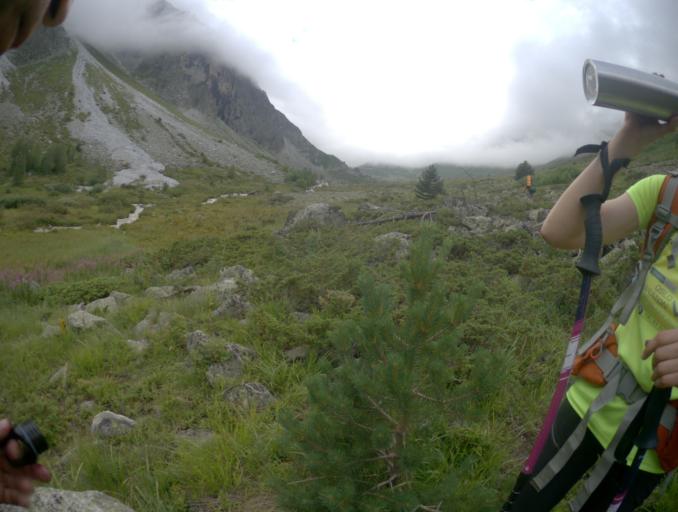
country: RU
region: Karachayevo-Cherkesiya
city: Uchkulan
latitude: 43.3357
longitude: 42.1254
